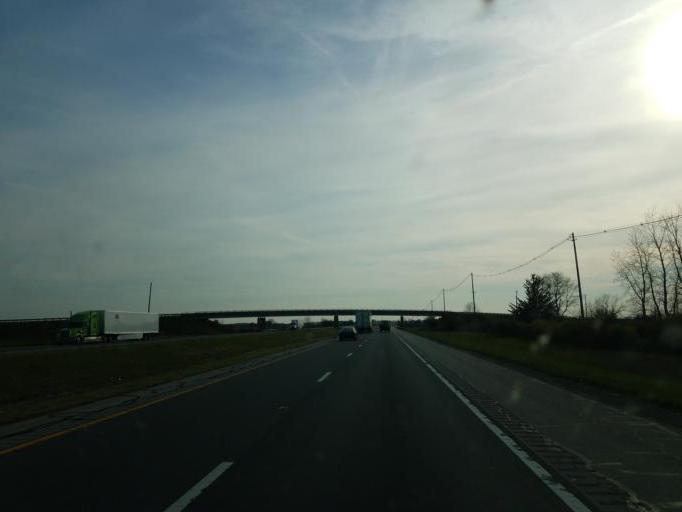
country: US
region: Ohio
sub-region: Fayette County
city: Jeffersonville
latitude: 39.6851
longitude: -83.4800
